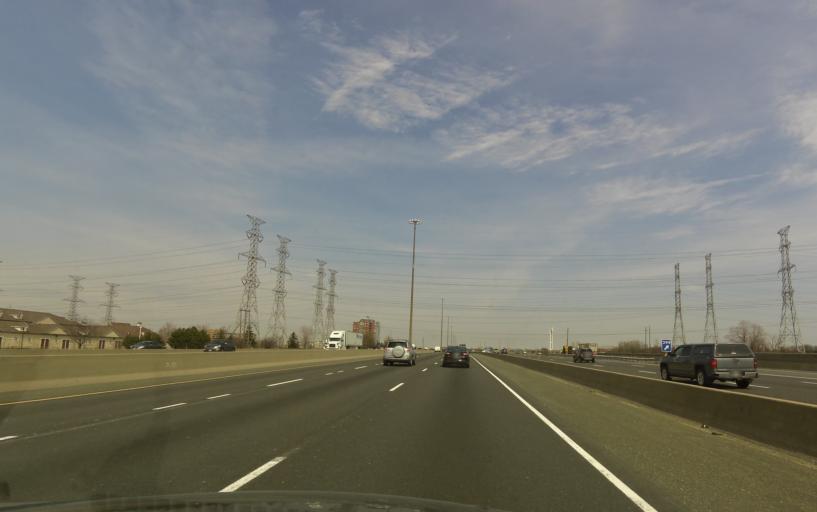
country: CA
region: Ontario
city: Ajax
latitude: 43.8355
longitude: -79.0779
